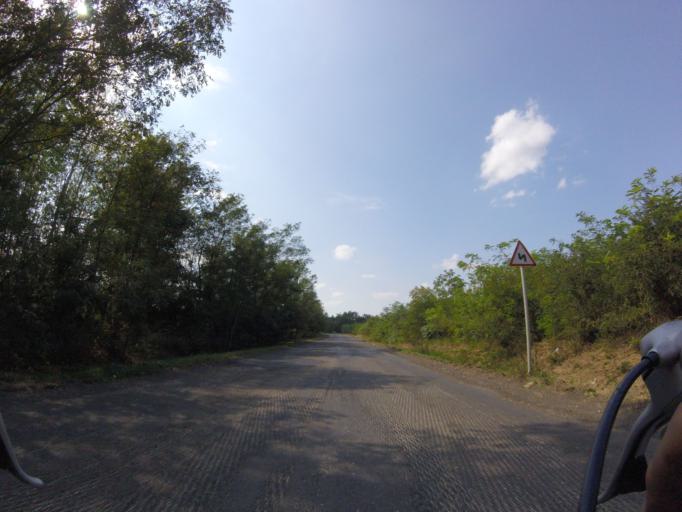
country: HU
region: Szabolcs-Szatmar-Bereg
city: Anarcs
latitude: 48.1637
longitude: 22.1248
